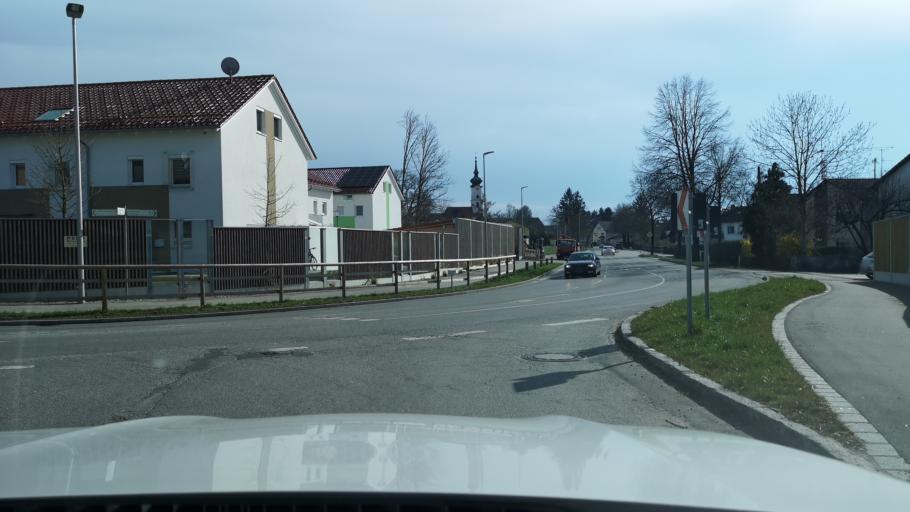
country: DE
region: Bavaria
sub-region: Upper Bavaria
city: Pliening
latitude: 48.2006
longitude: 11.8123
